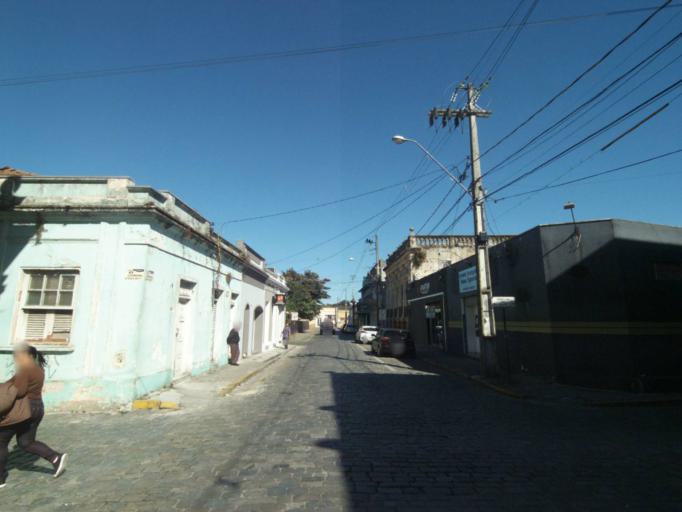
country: BR
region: Parana
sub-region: Paranagua
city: Paranagua
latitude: -25.5211
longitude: -48.5069
